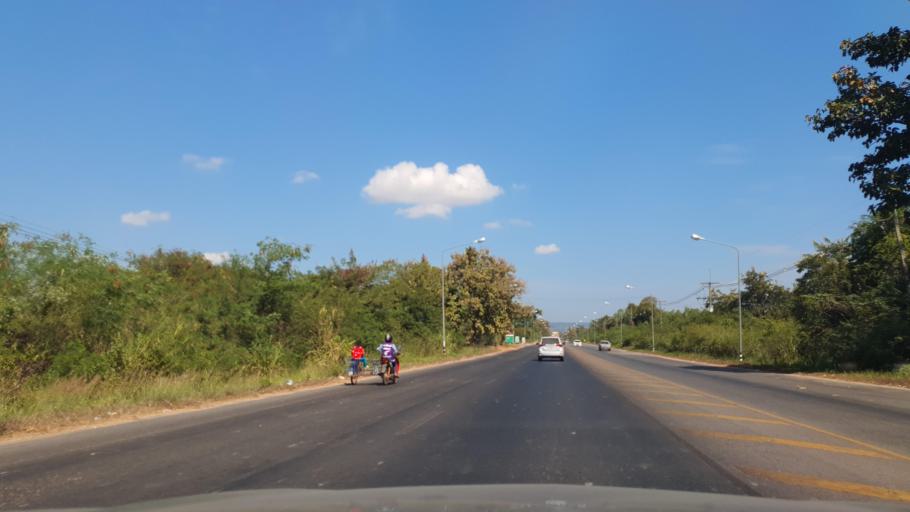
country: TH
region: Kalasin
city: Somdet
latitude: 16.7286
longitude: 103.7626
